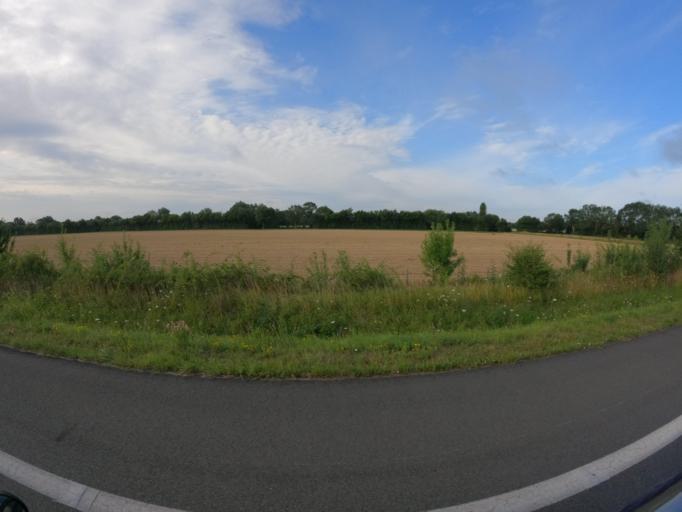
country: FR
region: Pays de la Loire
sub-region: Departement de Maine-et-Loire
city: Allonnes
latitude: 47.2869
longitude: 0.0037
